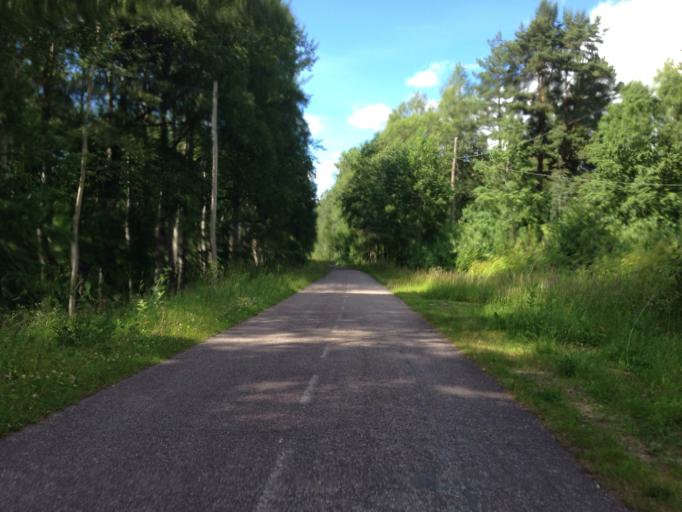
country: SE
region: Dalarna
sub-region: Ludvika Kommun
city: Ludvika
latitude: 60.1969
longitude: 15.1353
